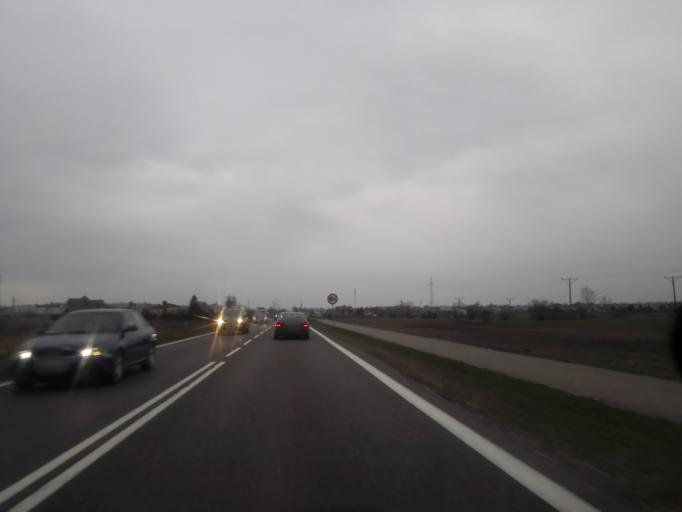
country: PL
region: Podlasie
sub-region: Powiat grajewski
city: Grajewo
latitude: 53.6528
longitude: 22.4810
